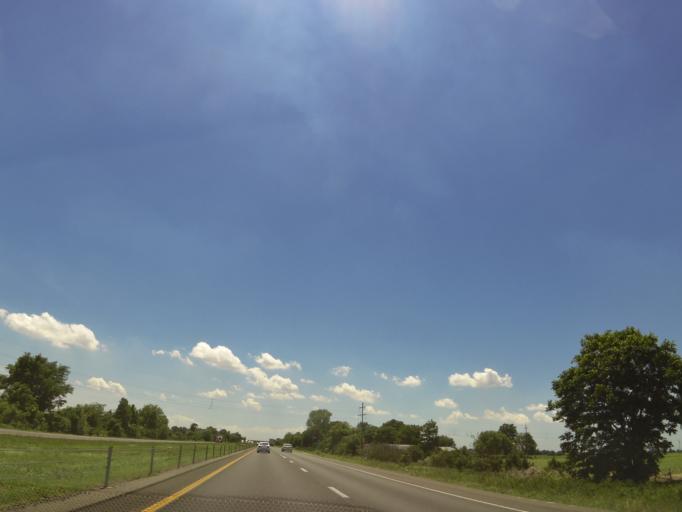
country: US
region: Missouri
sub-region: New Madrid County
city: Portageville
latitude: 36.4917
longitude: -89.6243
